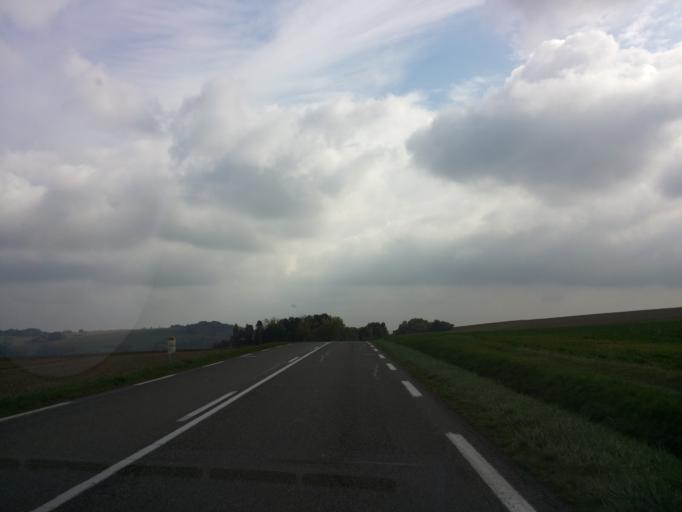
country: FR
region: Lorraine
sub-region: Departement de la Moselle
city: Vic-sur-Seille
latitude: 48.8061
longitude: 6.5482
